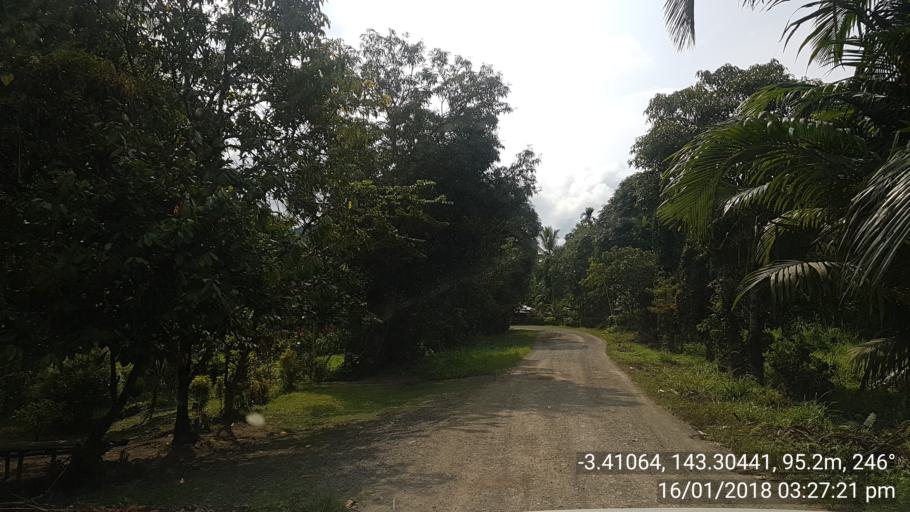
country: PG
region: East Sepik
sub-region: Wewak
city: Wewak
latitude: -3.4106
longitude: 143.3044
